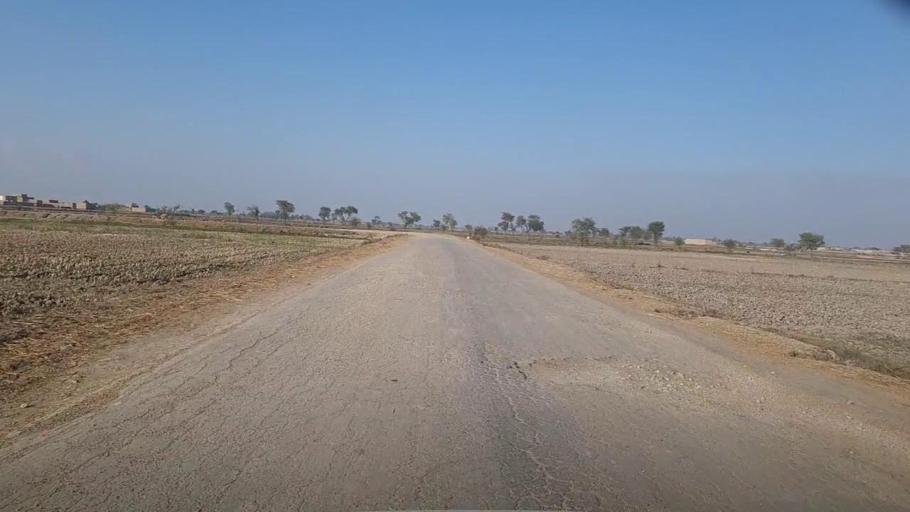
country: PK
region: Sindh
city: Phulji
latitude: 26.8650
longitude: 67.7946
